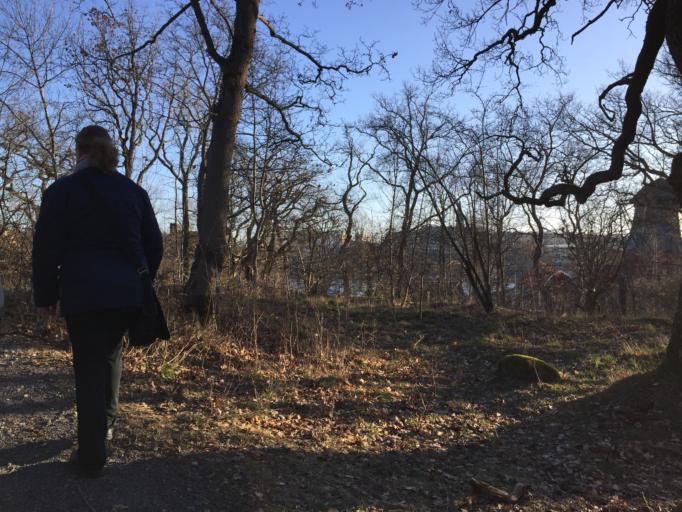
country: SE
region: Stockholm
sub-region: Stockholms Kommun
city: OEstermalm
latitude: 59.3212
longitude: 18.1165
